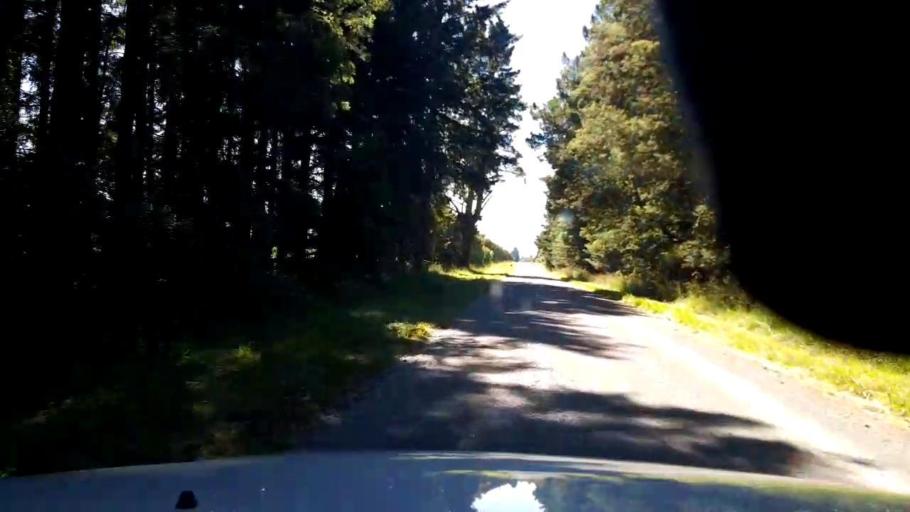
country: NZ
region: Canterbury
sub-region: Timaru District
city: Pleasant Point
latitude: -43.9689
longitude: 171.2322
